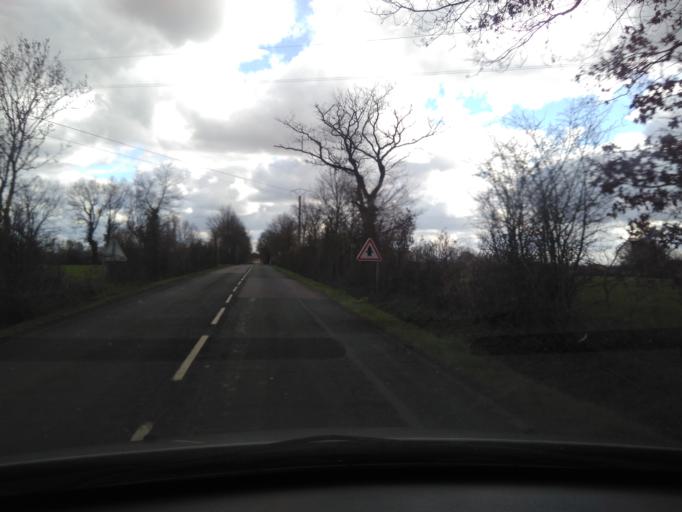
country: FR
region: Pays de la Loire
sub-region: Departement de la Vendee
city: Saint-Martin-des-Noyers
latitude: 46.7392
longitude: -1.1856
